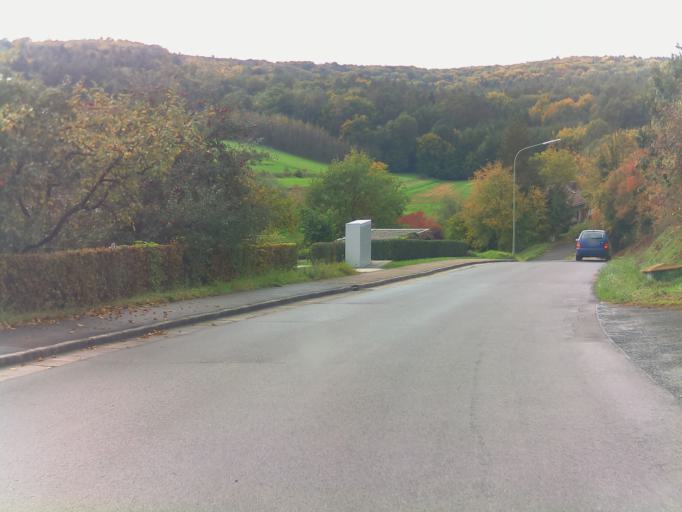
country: DE
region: Bavaria
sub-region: Upper Franconia
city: Priesendorf
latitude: 49.9233
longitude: 10.7422
